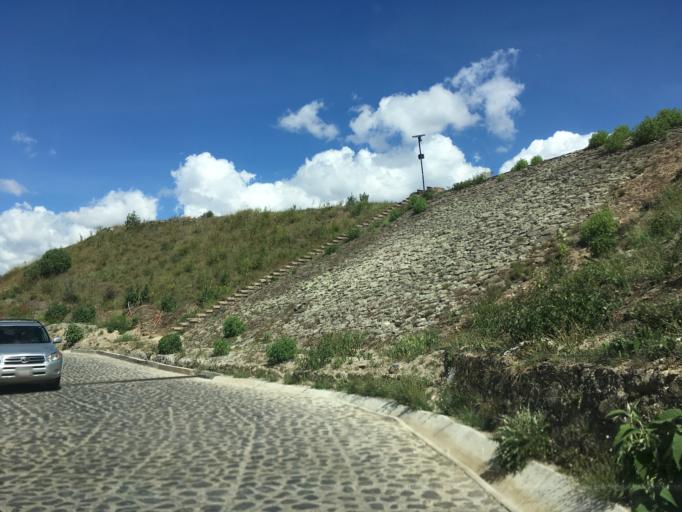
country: MX
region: Hidalgo
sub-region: Omitlan de Juarez
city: San Antonio el Paso
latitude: 20.2328
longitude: -98.5637
